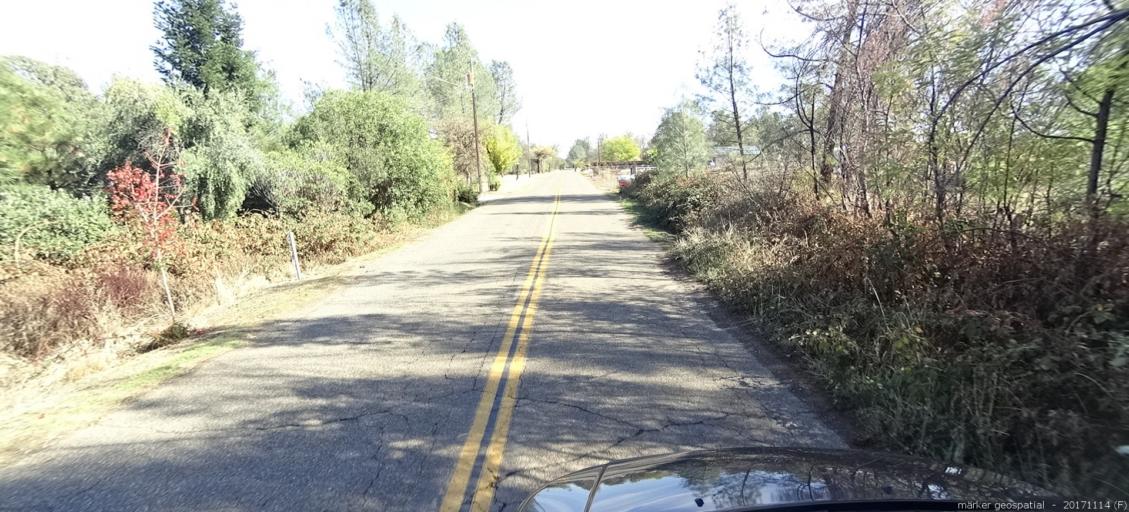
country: US
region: California
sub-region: Shasta County
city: Anderson
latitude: 40.4320
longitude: -122.4175
